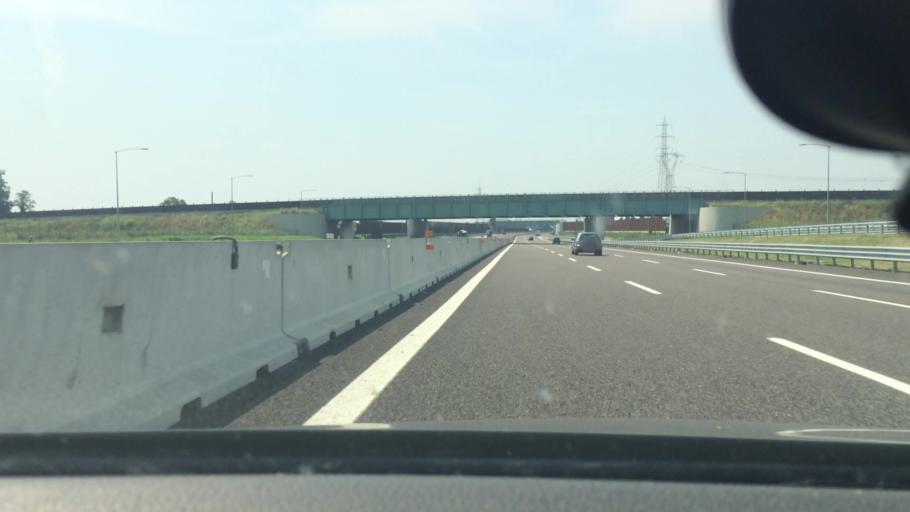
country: IT
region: Lombardy
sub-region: Provincia di Lodi
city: Merlino
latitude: 45.4230
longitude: 9.4197
